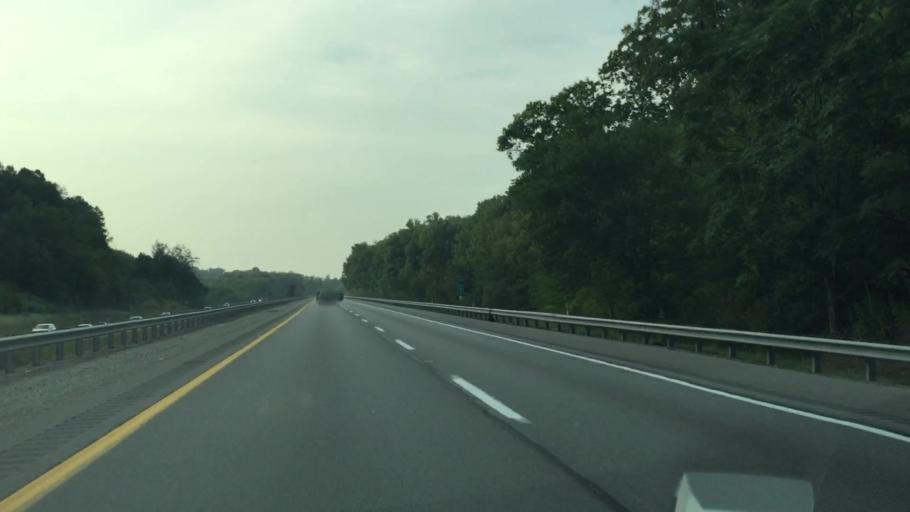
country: US
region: Pennsylvania
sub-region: Allegheny County
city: Franklin Park
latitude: 40.5778
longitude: -80.0948
